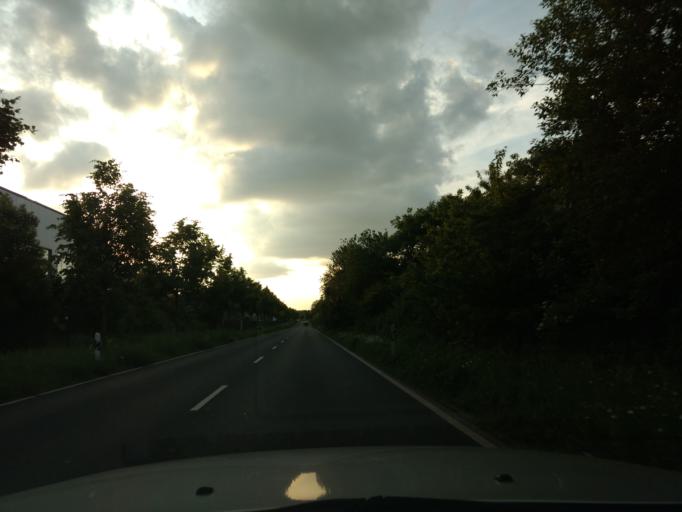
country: DE
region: North Rhine-Westphalia
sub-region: Regierungsbezirk Dusseldorf
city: Dusseldorf
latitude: 51.1659
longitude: 6.7485
